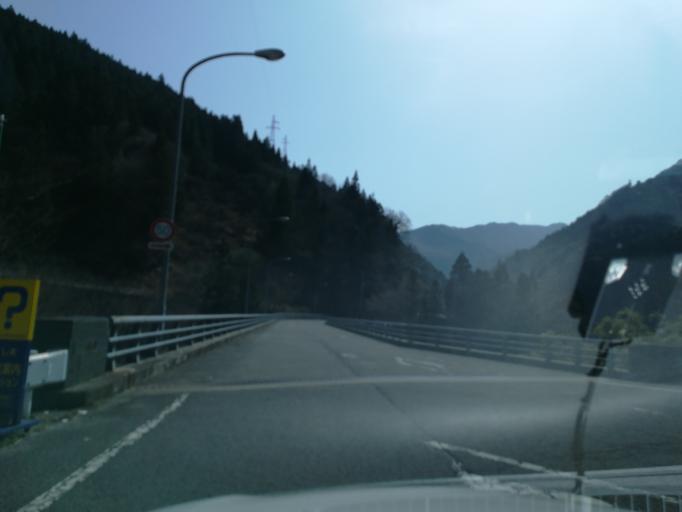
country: JP
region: Tokushima
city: Ikedacho
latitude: 33.8682
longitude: 133.9060
